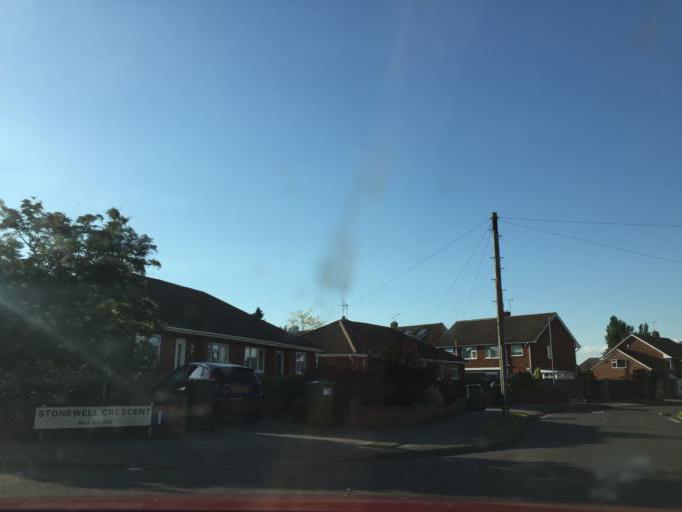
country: GB
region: England
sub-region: Warwickshire
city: Attleborough
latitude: 52.5030
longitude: -1.4328
